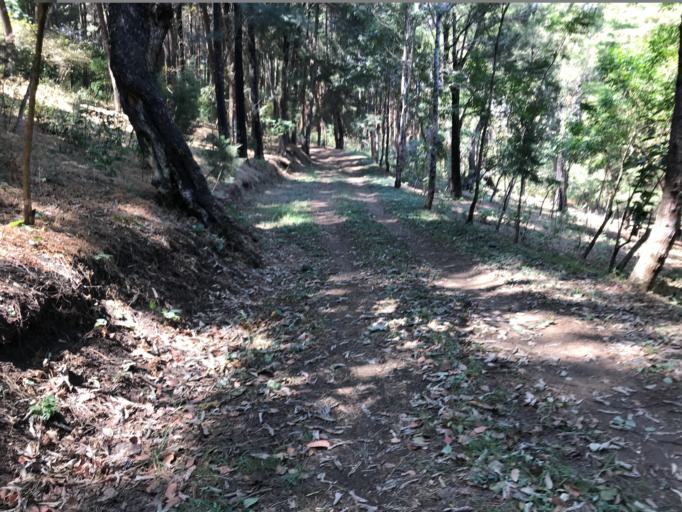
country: GT
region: Guatemala
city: Villa Canales
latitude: 14.4817
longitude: -90.5465
